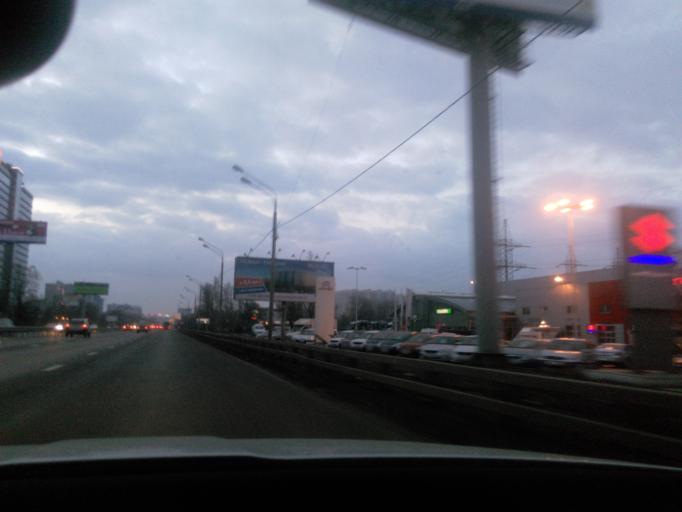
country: RU
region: Moscow
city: Khimki
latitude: 55.8973
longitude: 37.4254
